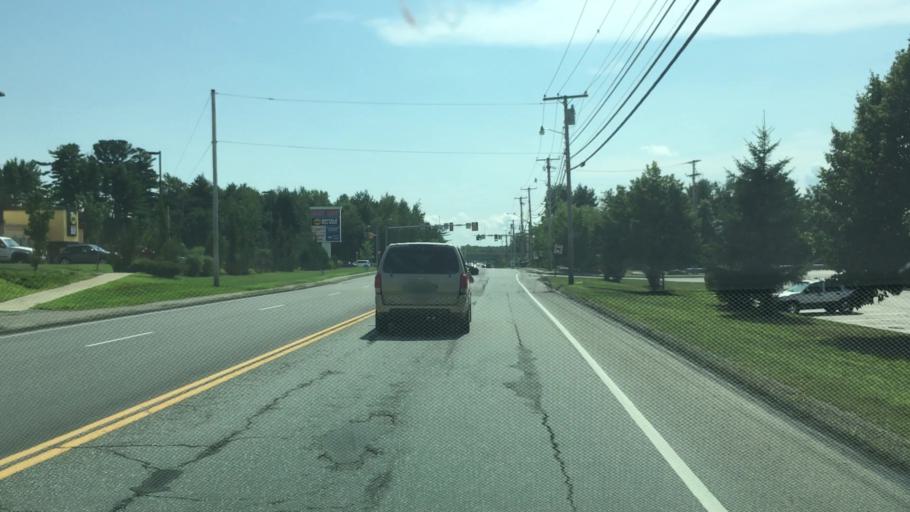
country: US
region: Maine
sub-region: Penobscot County
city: Brewer
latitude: 44.8271
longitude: -68.7564
